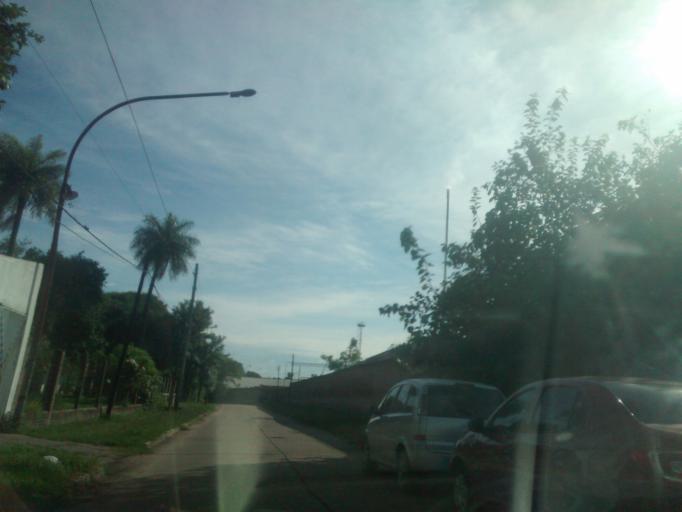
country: AR
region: Chaco
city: Puerto Tirol
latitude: -27.3719
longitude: -59.0892
